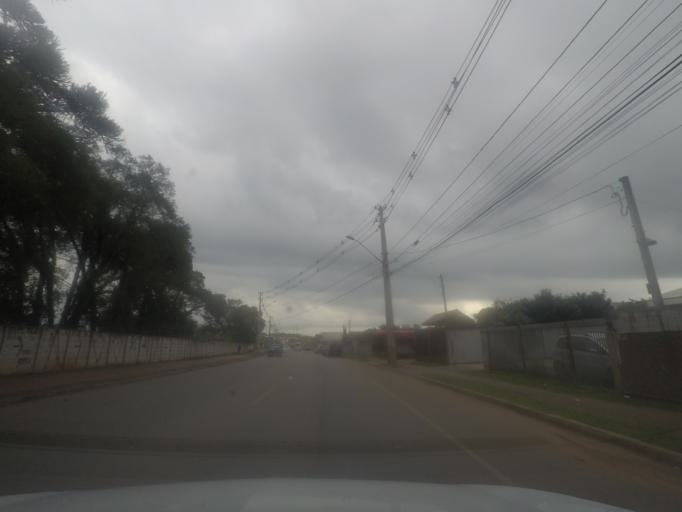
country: BR
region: Parana
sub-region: Sao Jose Dos Pinhais
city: Sao Jose dos Pinhais
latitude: -25.5592
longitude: -49.2614
